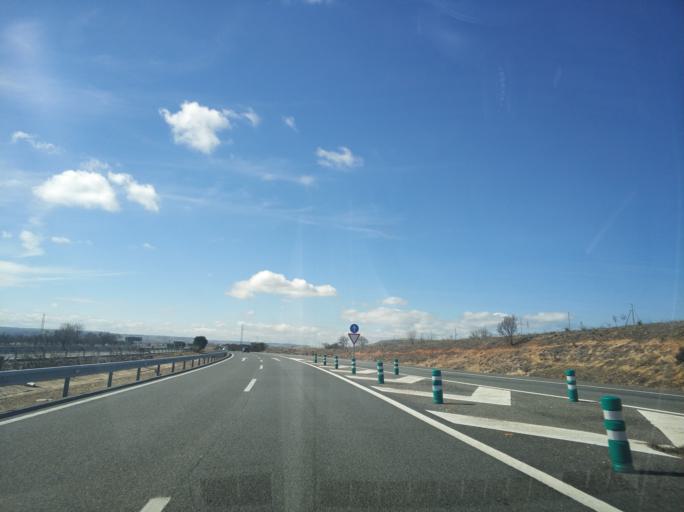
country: ES
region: Castille and Leon
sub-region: Provincia de Burgos
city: Villaquiran de los Infantes
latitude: 42.2216
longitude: -4.0036
